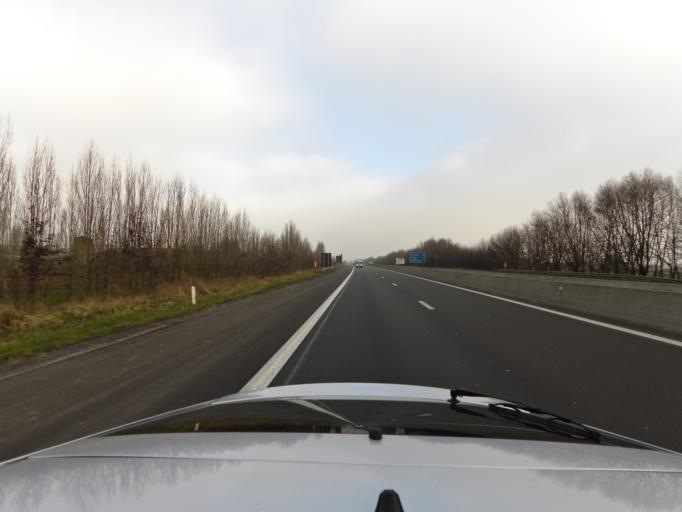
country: BE
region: Flanders
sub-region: Provincie West-Vlaanderen
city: Ardooie
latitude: 50.9804
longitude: 3.1777
